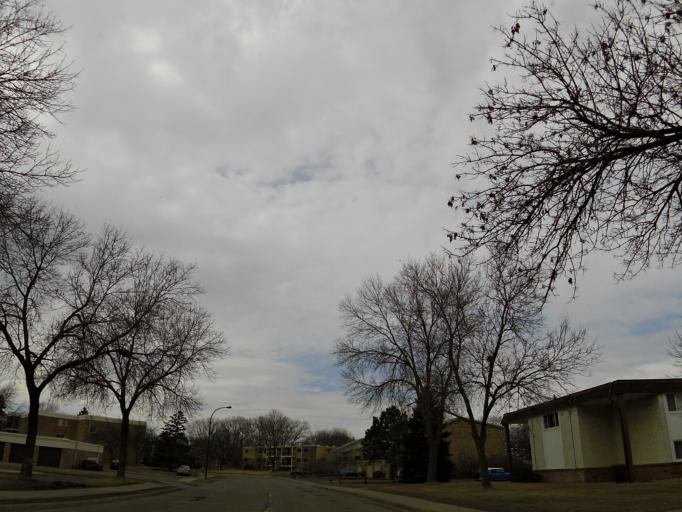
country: US
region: Minnesota
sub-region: Hennepin County
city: Edina
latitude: 44.8684
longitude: -93.3351
